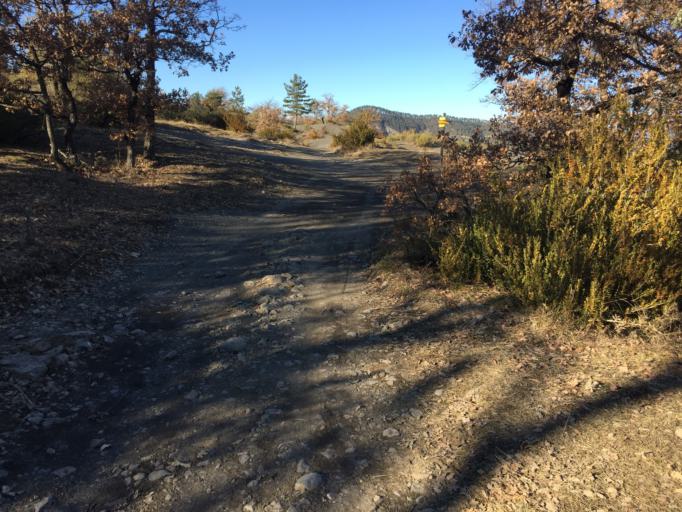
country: FR
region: Provence-Alpes-Cote d'Azur
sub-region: Departement des Alpes-de-Haute-Provence
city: Digne-les-Bains
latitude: 44.0794
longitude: 6.2718
